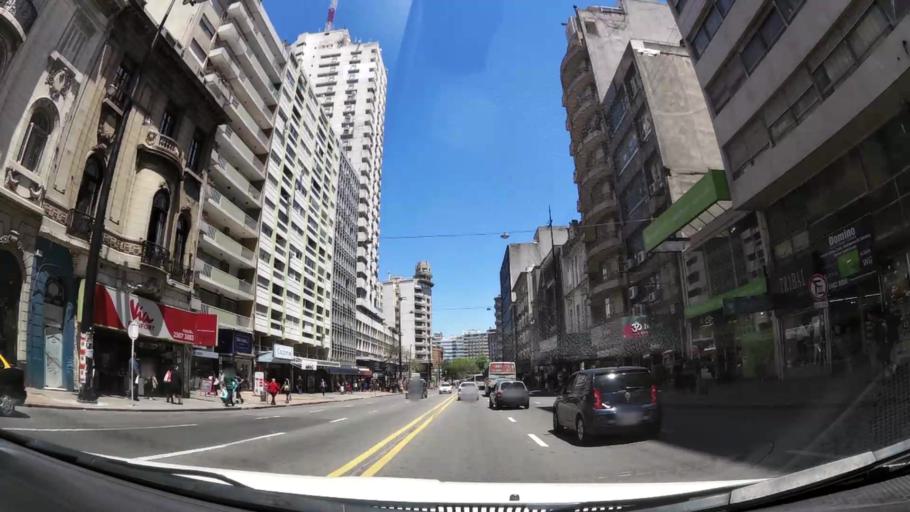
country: UY
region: Montevideo
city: Montevideo
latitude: -34.9049
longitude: -56.1836
